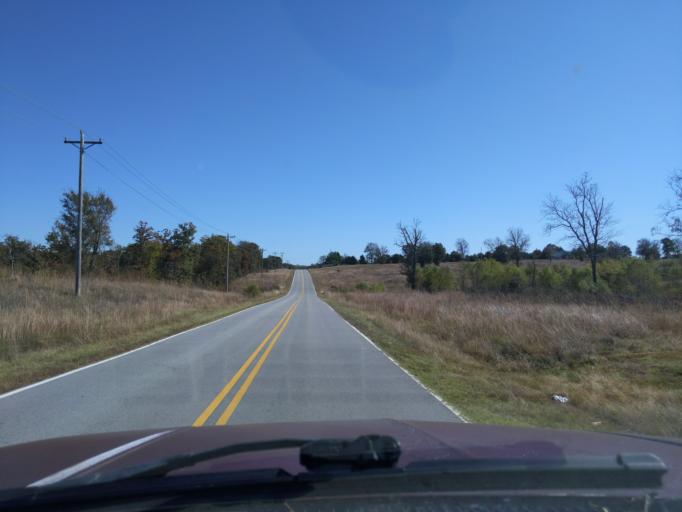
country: US
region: Oklahoma
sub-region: Creek County
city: Bristow
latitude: 35.7119
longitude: -96.3940
